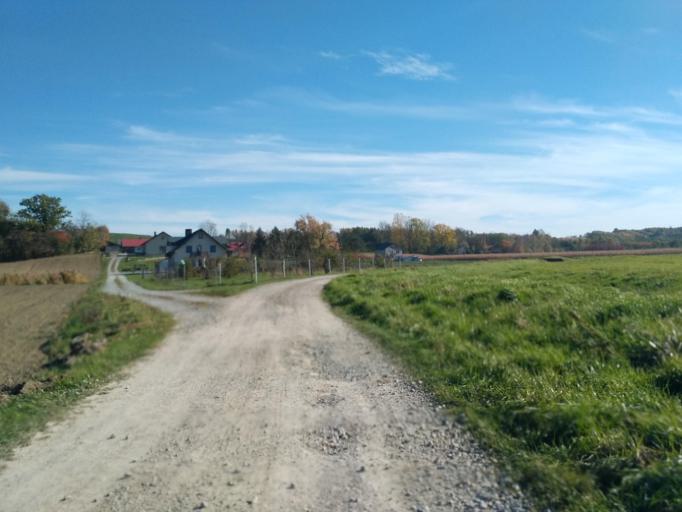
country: PL
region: Subcarpathian Voivodeship
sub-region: Powiat ropczycko-sedziszowski
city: Iwierzyce
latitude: 50.0121
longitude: 21.7560
